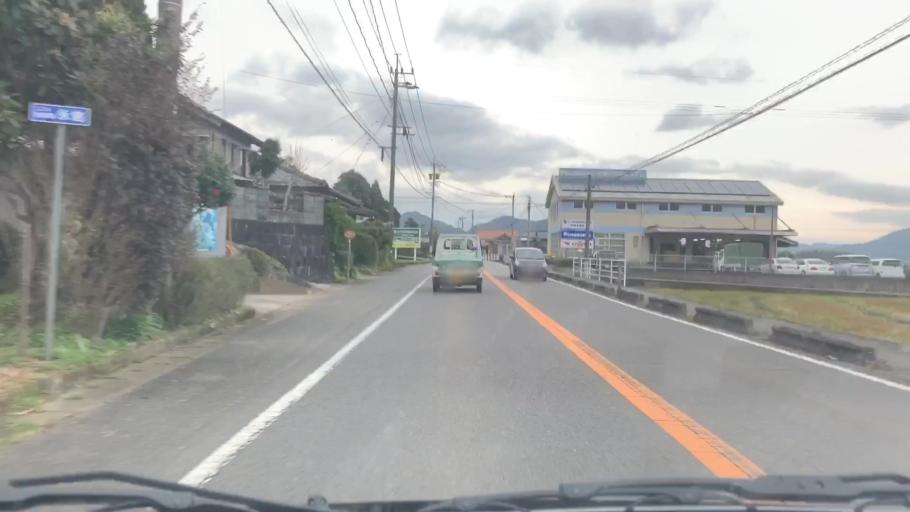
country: JP
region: Saga Prefecture
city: Takeocho-takeo
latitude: 33.1815
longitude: 130.0424
